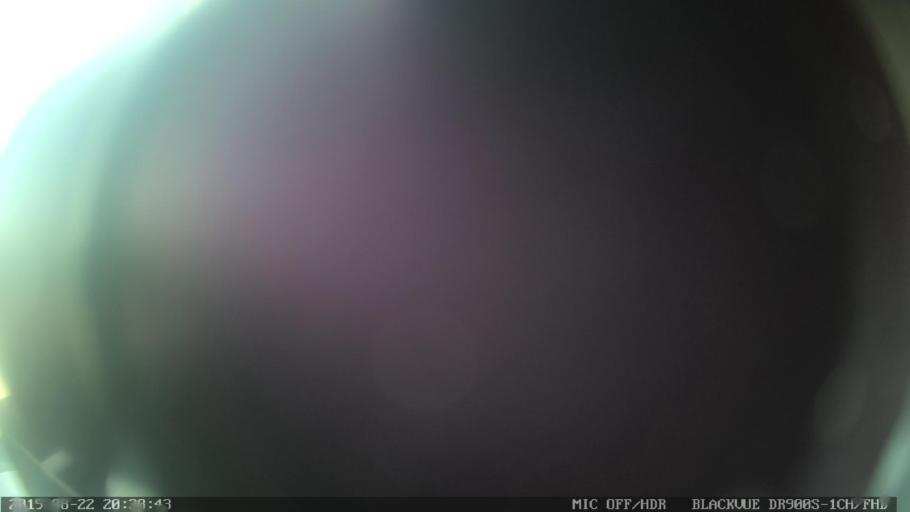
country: PT
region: Castelo Branco
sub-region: Proenca-A-Nova
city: Proenca-a-Nova
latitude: 39.6876
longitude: -7.7534
